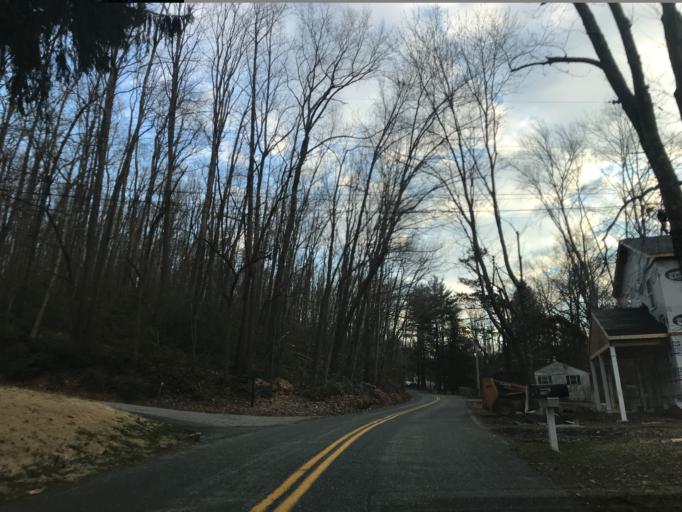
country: US
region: Maryland
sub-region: Harford County
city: Jarrettsville
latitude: 39.6278
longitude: -76.4196
